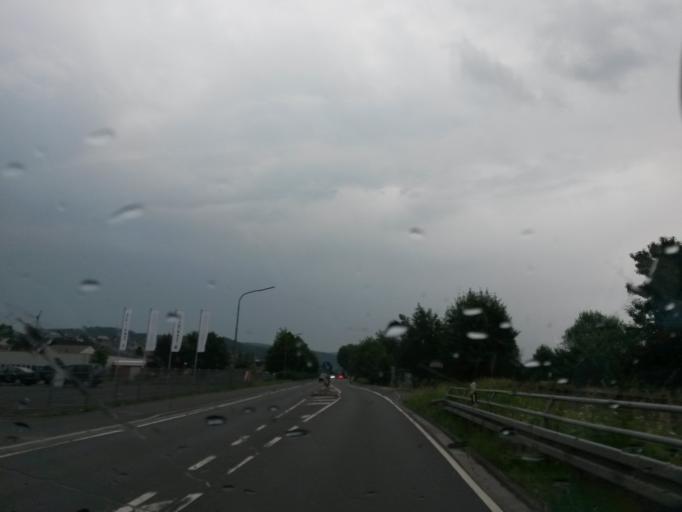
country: DE
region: North Rhine-Westphalia
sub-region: Regierungsbezirk Koln
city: Overath
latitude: 50.9556
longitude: 7.3118
